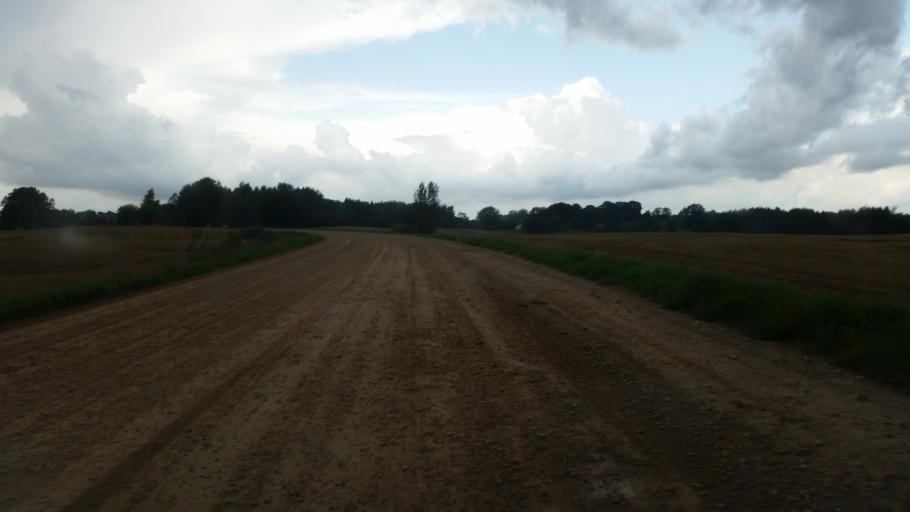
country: LV
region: Vecumnieki
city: Vecumnieki
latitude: 56.4252
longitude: 24.4923
